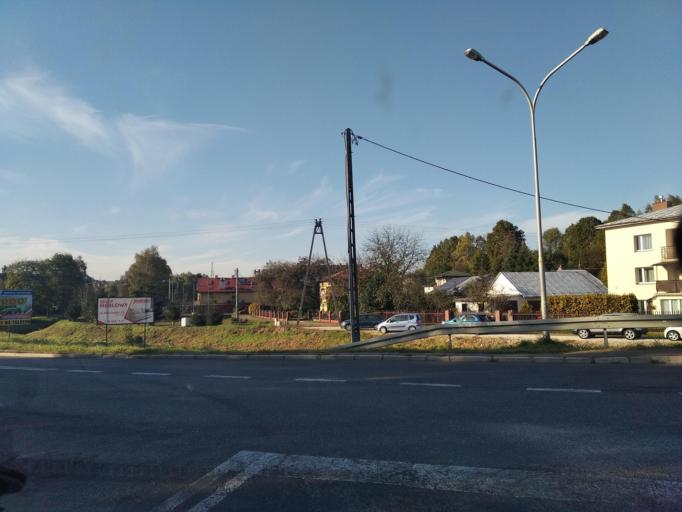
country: PL
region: Subcarpathian Voivodeship
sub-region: Powiat brzozowski
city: Brzozow
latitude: 49.6861
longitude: 22.0297
